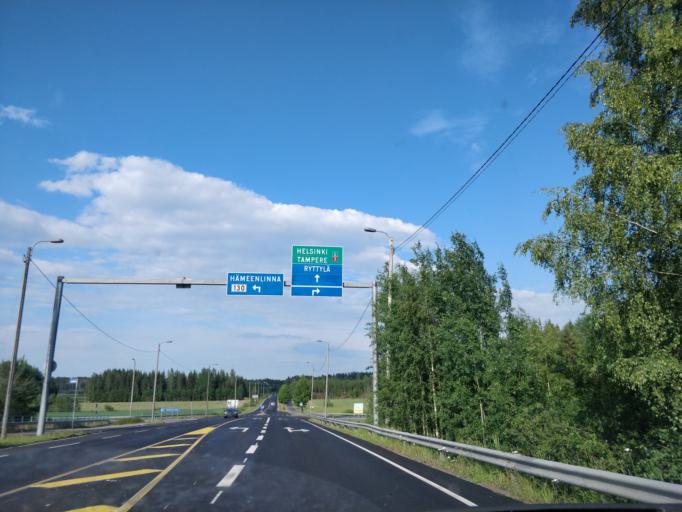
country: FI
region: Haeme
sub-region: Haemeenlinna
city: Tervakoski
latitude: 60.8186
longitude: 24.6421
